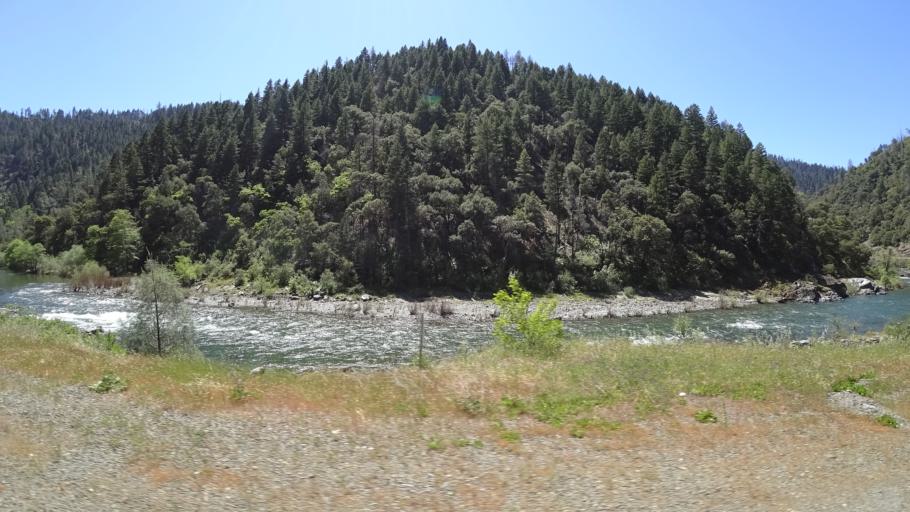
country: US
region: California
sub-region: Trinity County
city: Hayfork
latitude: 40.7668
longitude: -123.2931
